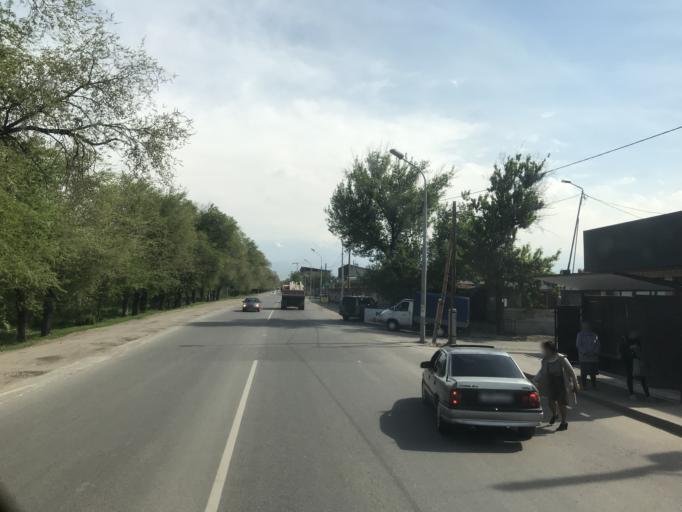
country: KZ
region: Almaty Qalasy
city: Almaty
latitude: 43.2475
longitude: 76.8038
